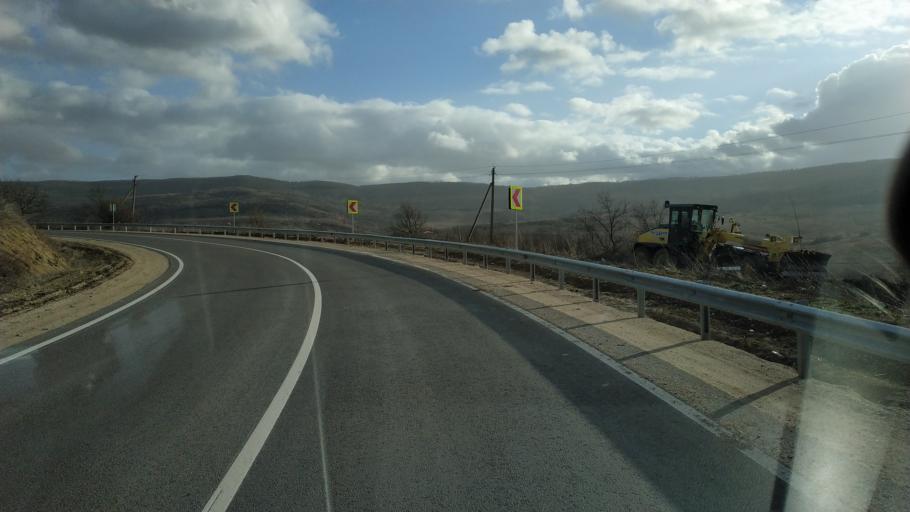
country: MD
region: Calarasi
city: Calarasi
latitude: 47.2979
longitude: 28.1526
